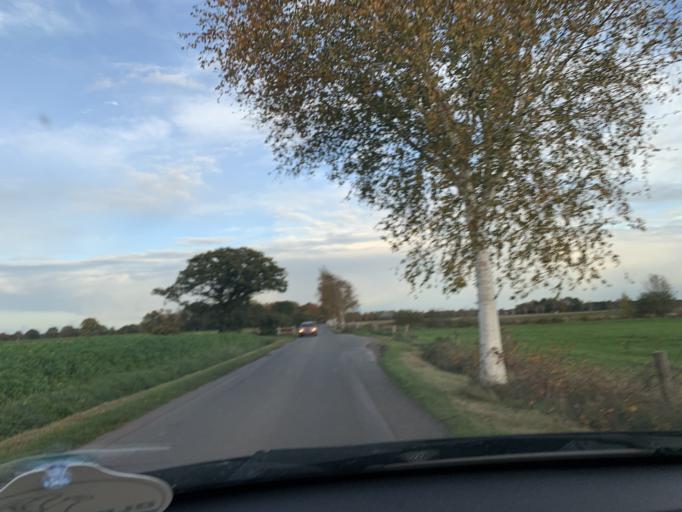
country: DE
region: Lower Saxony
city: Wiefelstede
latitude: 53.2524
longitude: 8.0815
